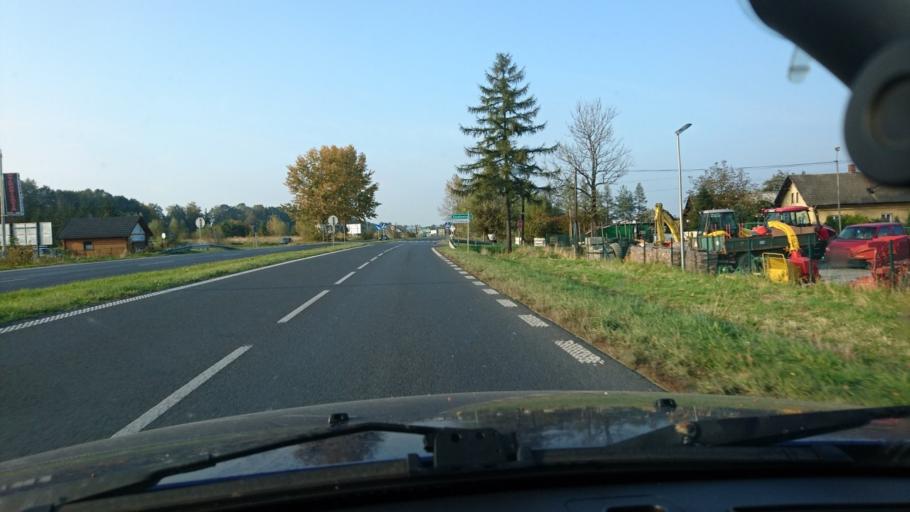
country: PL
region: Silesian Voivodeship
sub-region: Powiat cieszynski
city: Ustron
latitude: 49.7354
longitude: 18.7912
